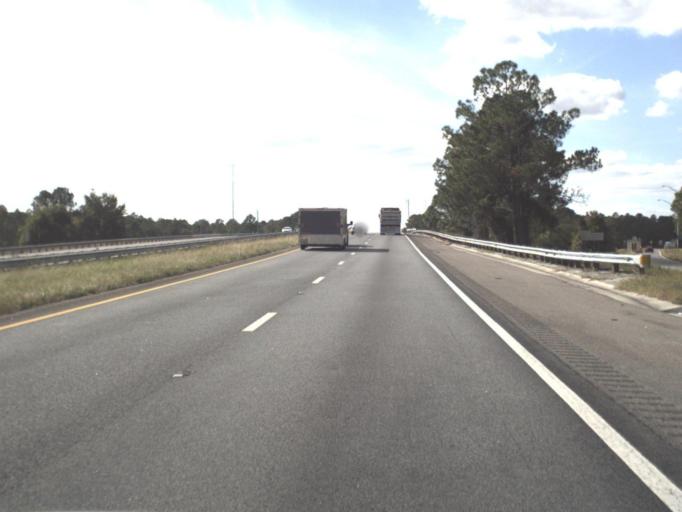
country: US
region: Florida
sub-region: Orange County
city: Christmas
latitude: 28.4527
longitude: -80.9757
